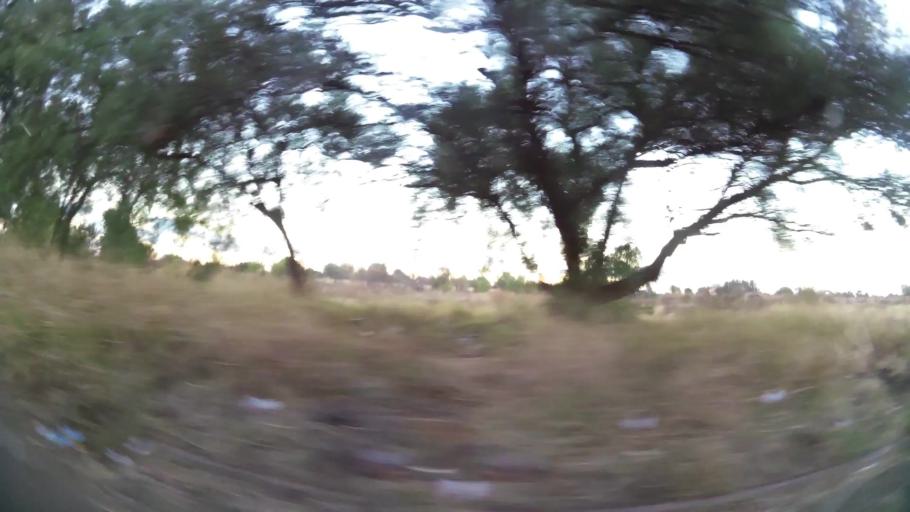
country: ZA
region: Northern Cape
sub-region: Frances Baard District Municipality
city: Kimberley
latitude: -28.7273
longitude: 24.7646
